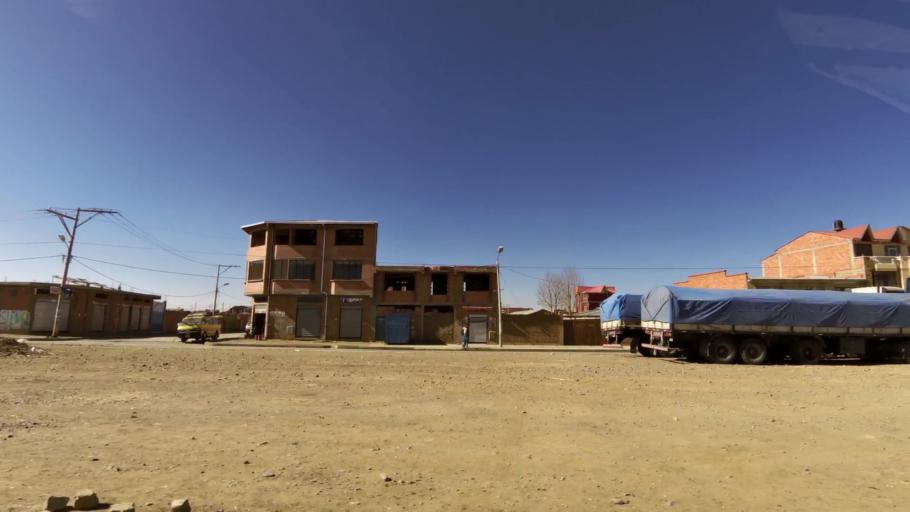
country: BO
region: La Paz
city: La Paz
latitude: -16.5384
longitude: -68.2256
